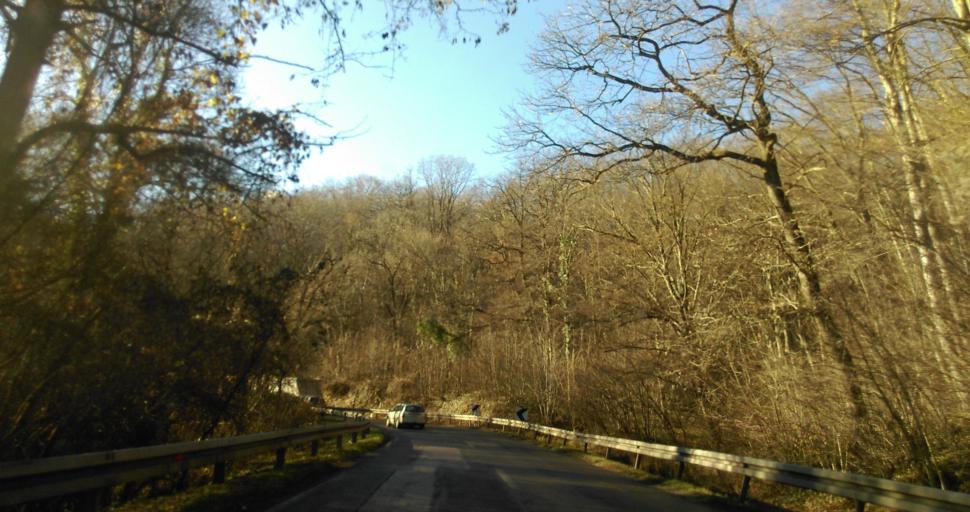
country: RS
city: Vrdnik
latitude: 45.1719
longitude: 19.8273
